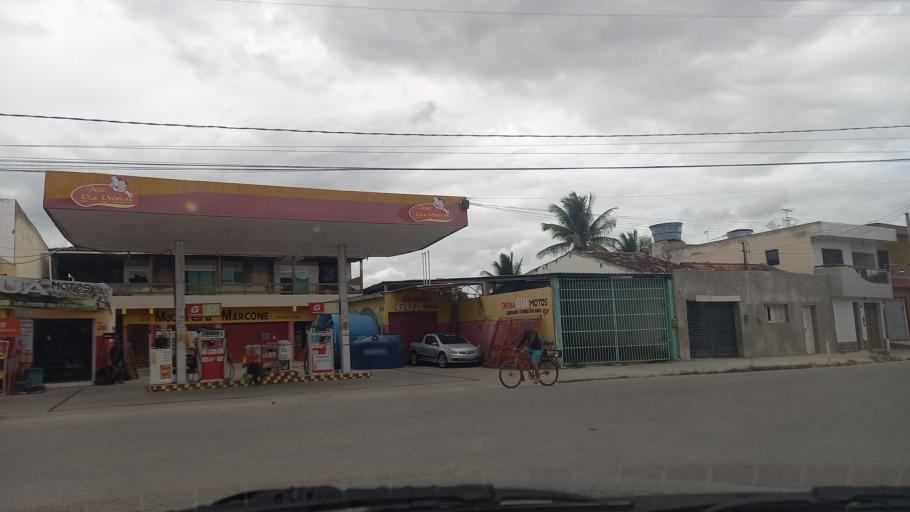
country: BR
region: Pernambuco
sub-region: Caruaru
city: Caruaru
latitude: -8.3305
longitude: -36.1354
